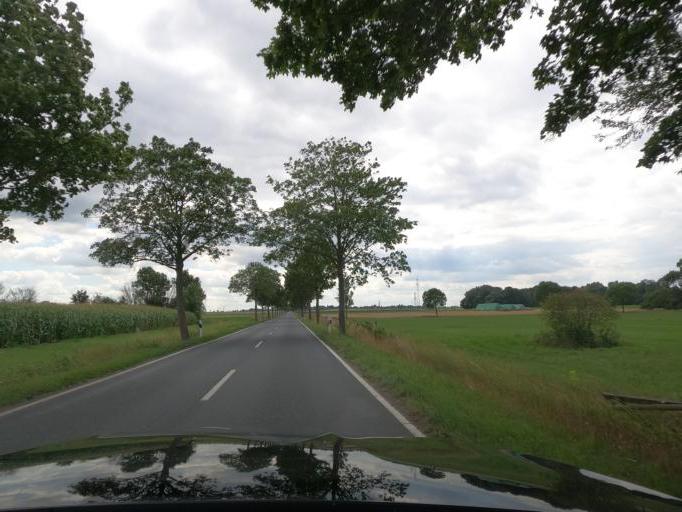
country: DE
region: Lower Saxony
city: Lehrte
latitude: 52.3356
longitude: 10.0276
